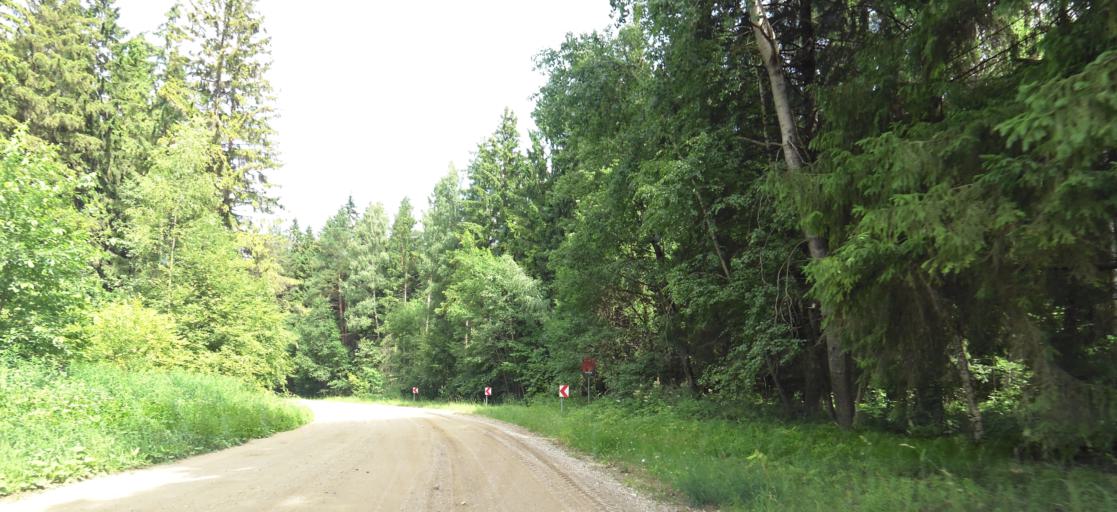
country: LT
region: Panevezys
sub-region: Birzai
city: Birzai
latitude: 56.2683
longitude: 24.7616
